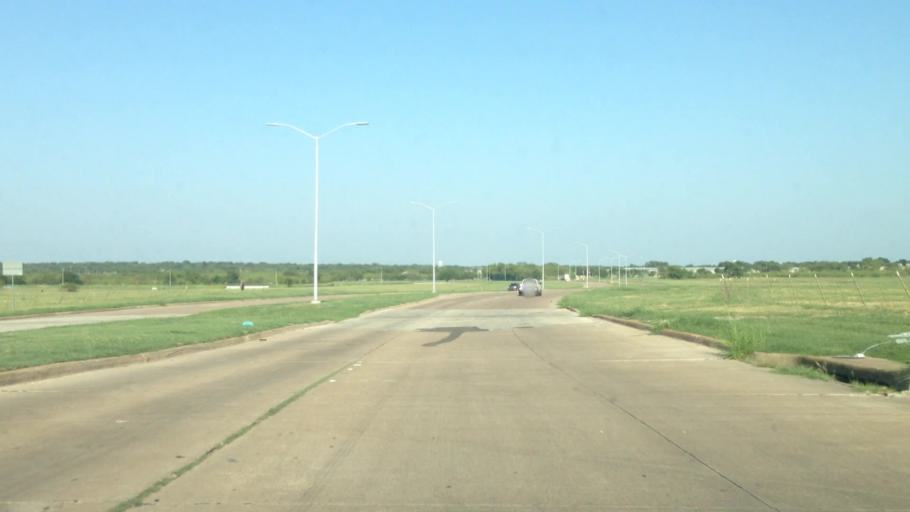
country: US
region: Texas
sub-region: Tarrant County
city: Haltom City
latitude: 32.8105
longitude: -97.3074
